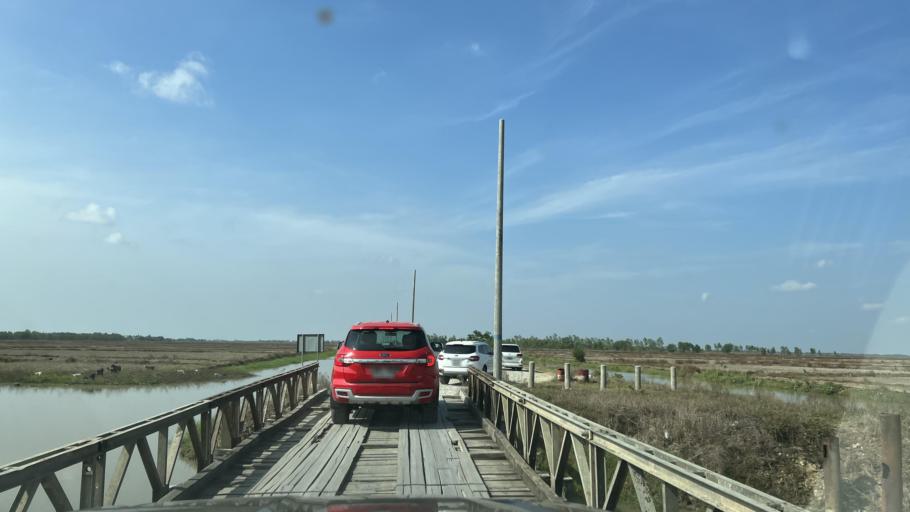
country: MM
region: Ayeyarwady
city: Pyapon
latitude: 16.0690
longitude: 95.6187
